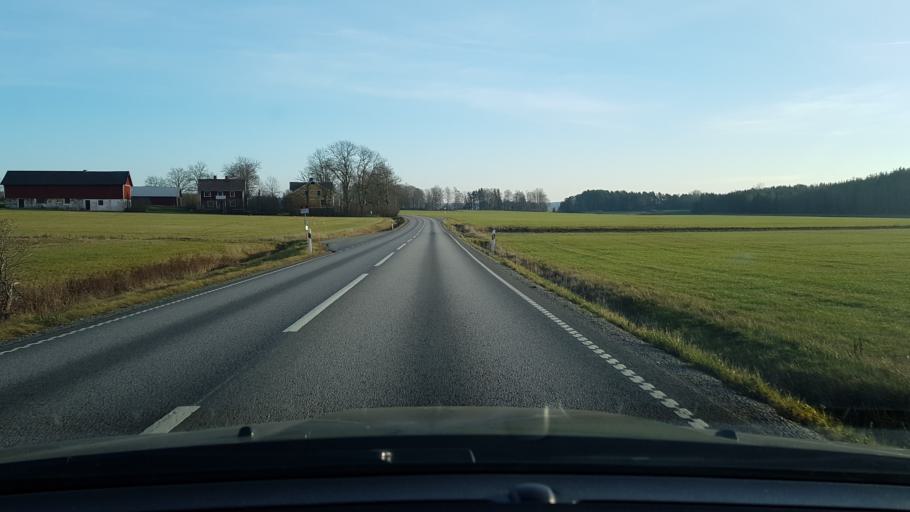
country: SE
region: Stockholm
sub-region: Norrtalje Kommun
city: Nykvarn
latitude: 59.7431
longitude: 18.1298
